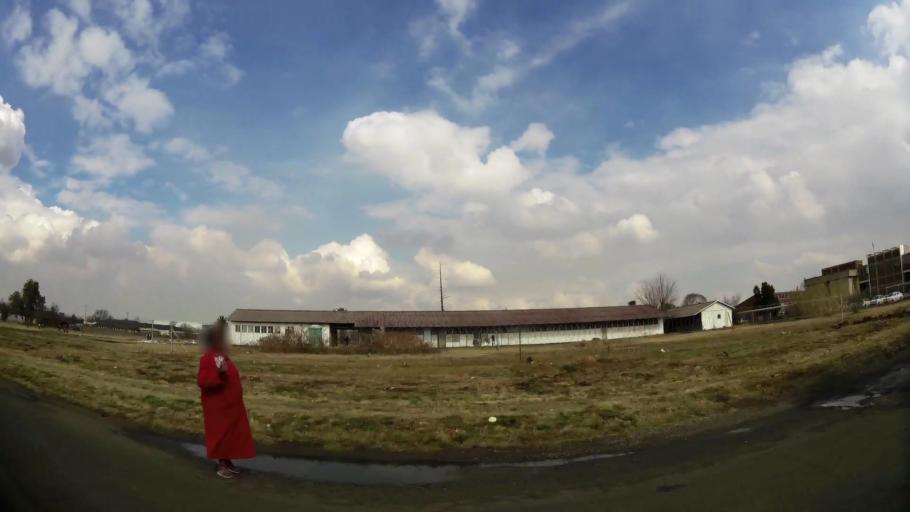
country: ZA
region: Gauteng
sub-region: Sedibeng District Municipality
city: Vereeniging
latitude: -26.6669
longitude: 27.9186
